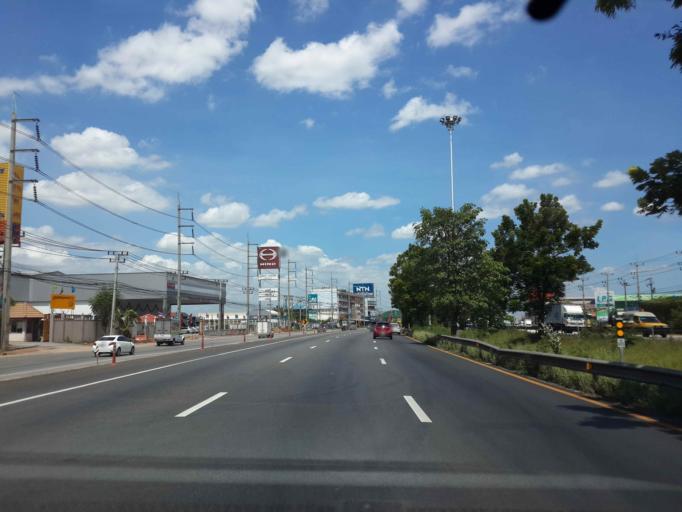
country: TH
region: Samut Sakhon
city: Samut Sakhon
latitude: 13.5929
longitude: 100.3381
